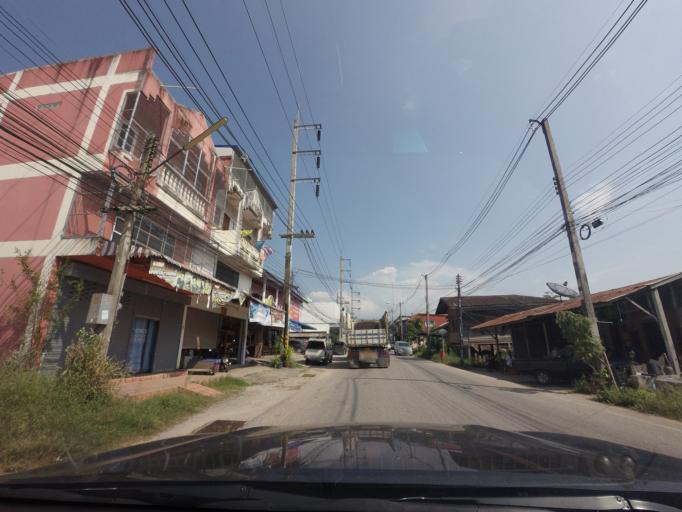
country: TH
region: Phitsanulok
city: Nakhon Thai
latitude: 17.1019
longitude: 100.8364
